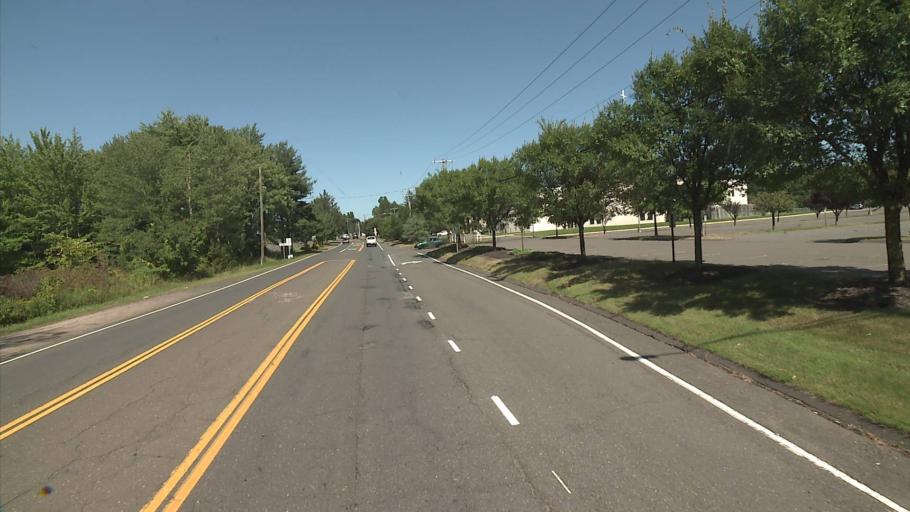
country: US
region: Connecticut
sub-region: Hartford County
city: Blue Hills
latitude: 41.8335
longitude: -72.7010
